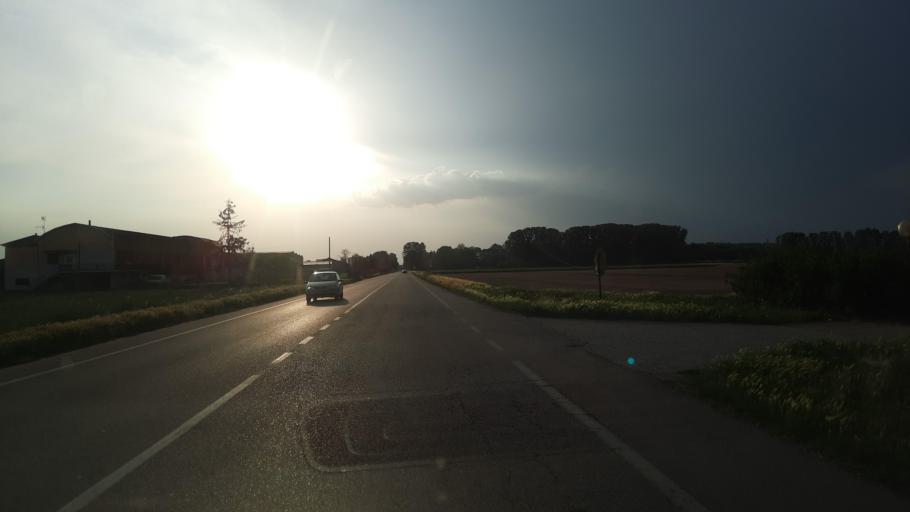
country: IT
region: Lombardy
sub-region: Provincia di Pavia
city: Mortara
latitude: 45.2463
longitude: 8.7654
